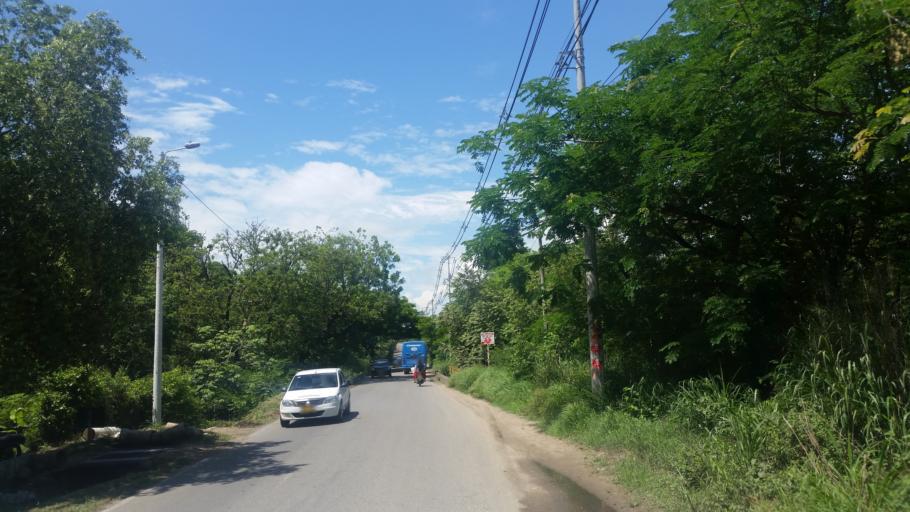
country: CO
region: Huila
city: Neiva
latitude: 2.9838
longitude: -75.2804
